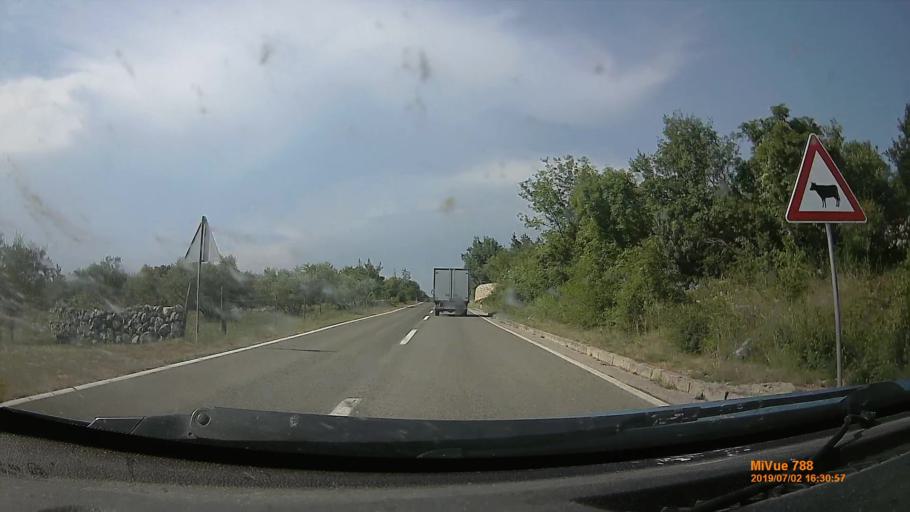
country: HR
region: Primorsko-Goranska
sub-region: Grad Krk
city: Krk
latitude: 45.0483
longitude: 14.4887
